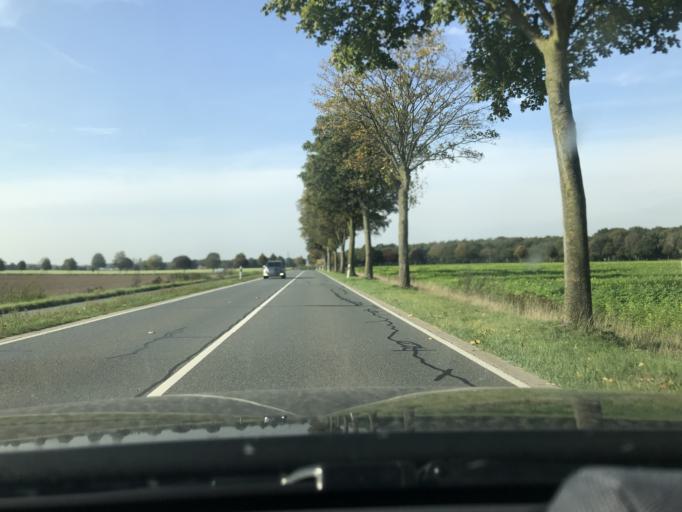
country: DE
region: North Rhine-Westphalia
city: Kalkar
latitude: 51.7371
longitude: 6.2525
